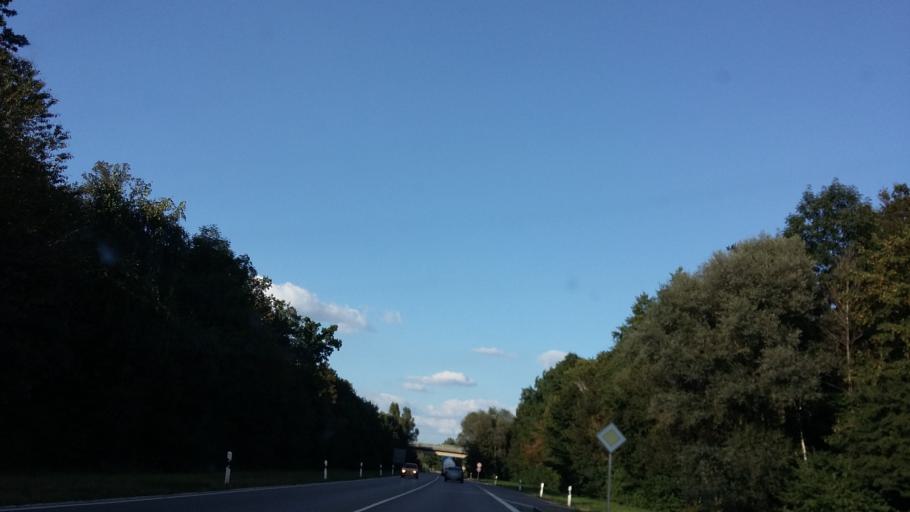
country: DE
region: Bavaria
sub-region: Swabia
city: Holzheim
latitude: 48.4070
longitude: 10.0811
